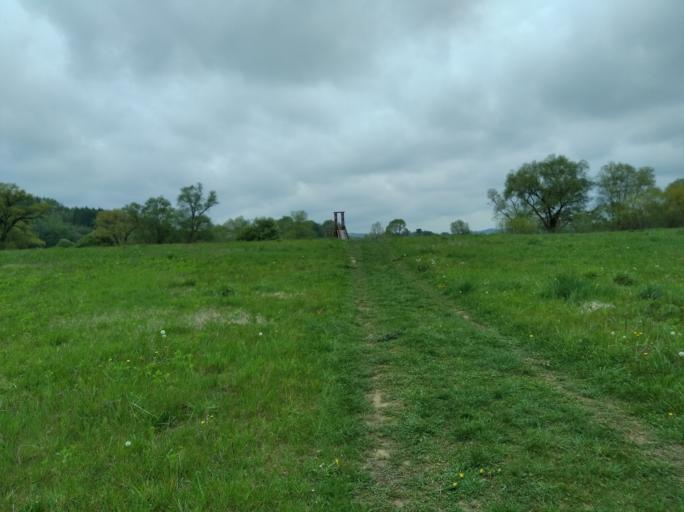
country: PL
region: Subcarpathian Voivodeship
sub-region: Powiat brzozowski
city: Nozdrzec
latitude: 49.7465
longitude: 22.2244
